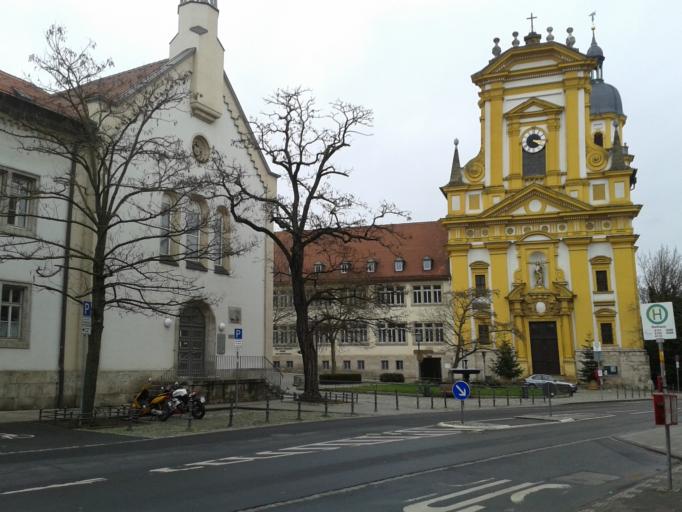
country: DE
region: Bavaria
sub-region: Regierungsbezirk Unterfranken
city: Kitzingen
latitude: 49.7395
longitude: 10.1618
